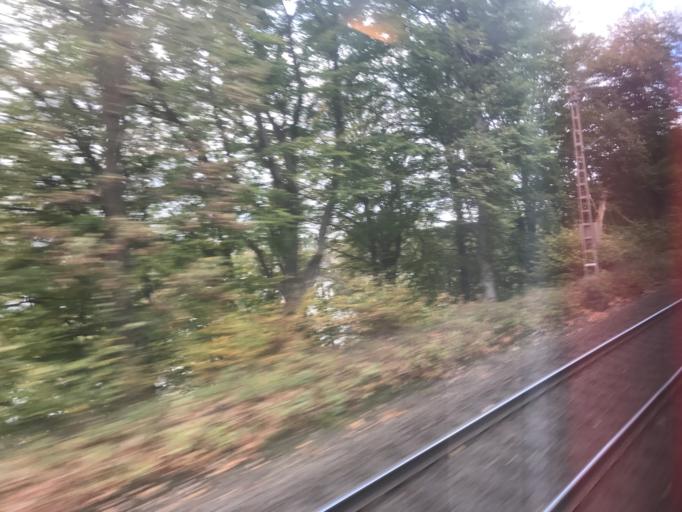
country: DE
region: North Rhine-Westphalia
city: Gevelsberg
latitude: 51.3159
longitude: 7.3435
